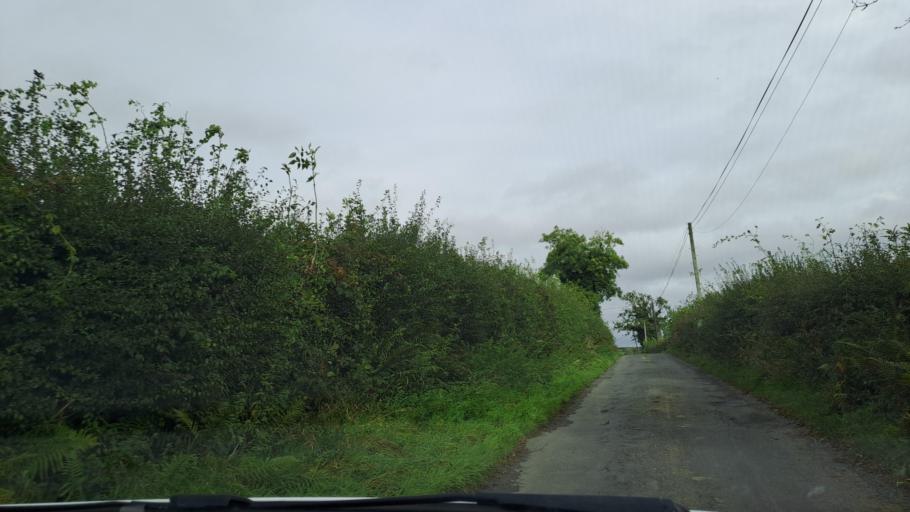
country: IE
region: Ulster
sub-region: An Cabhan
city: Bailieborough
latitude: 54.0079
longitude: -6.9494
